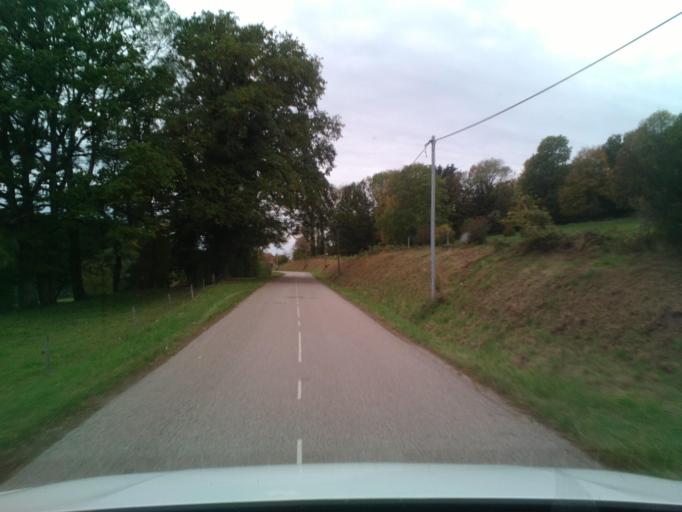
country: FR
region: Lorraine
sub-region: Departement des Vosges
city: Senones
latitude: 48.3365
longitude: 7.0142
